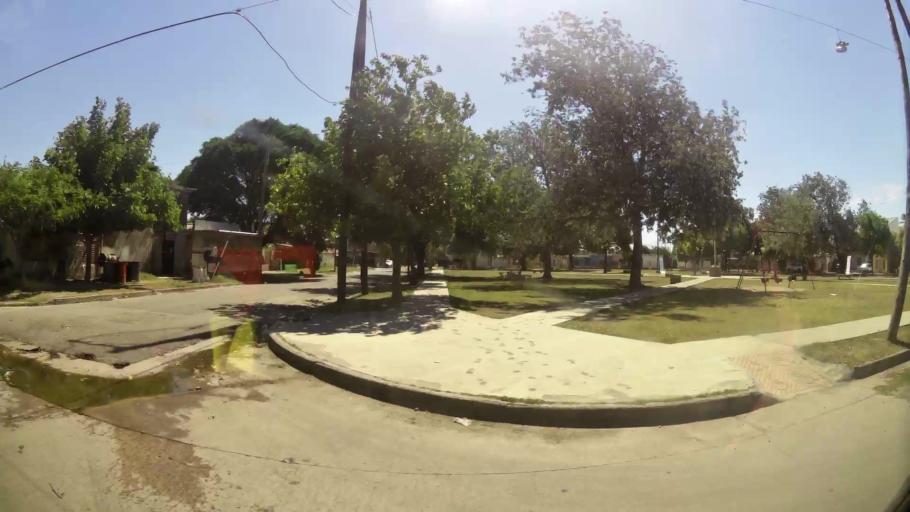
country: AR
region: Cordoba
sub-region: Departamento de Capital
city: Cordoba
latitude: -31.3673
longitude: -64.1357
